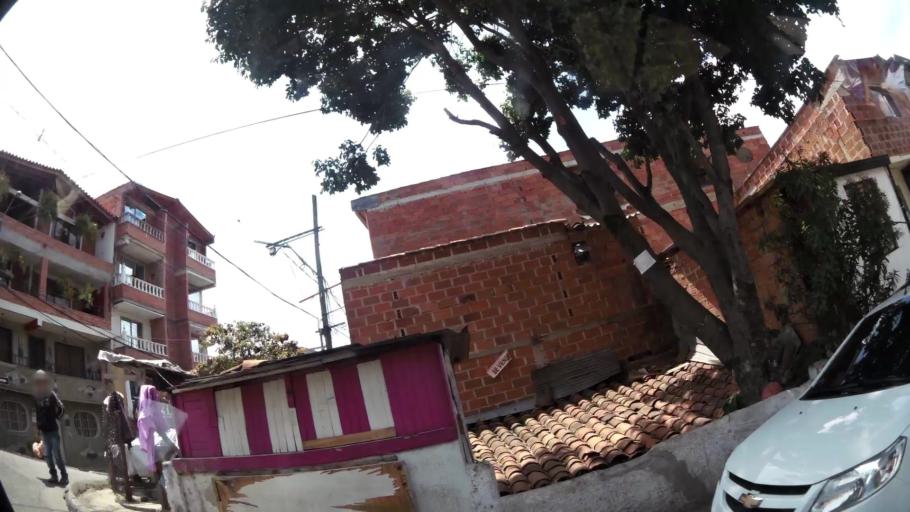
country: CO
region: Antioquia
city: Bello
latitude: 6.3488
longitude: -75.5622
